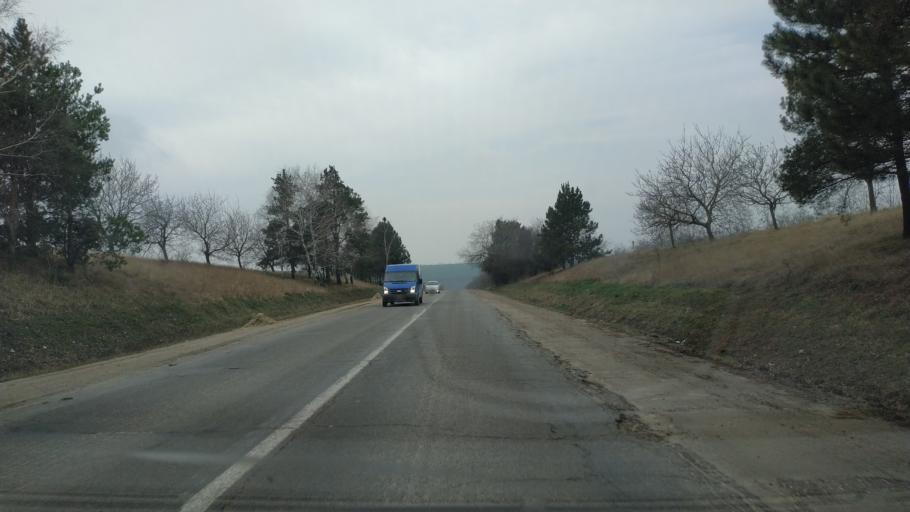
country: MD
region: Cahul
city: Cahul
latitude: 45.9465
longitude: 28.3099
